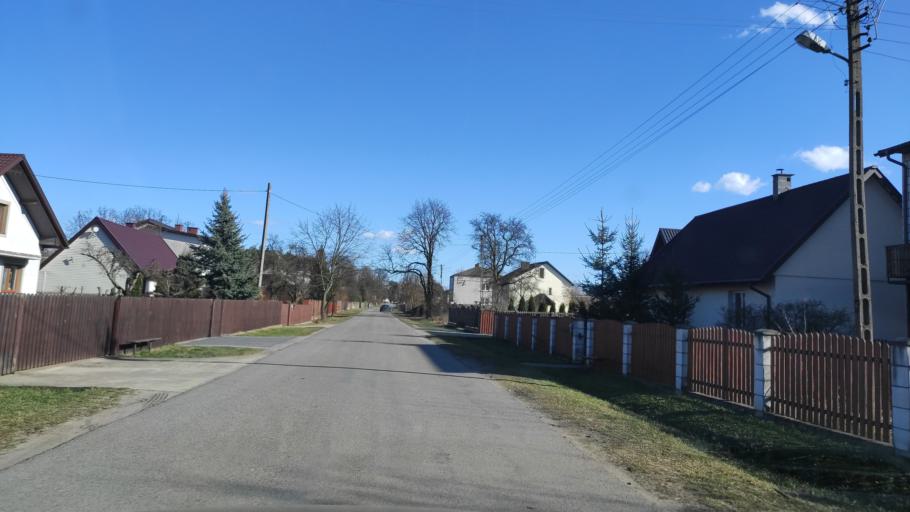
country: PL
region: Masovian Voivodeship
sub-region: Powiat radomski
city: Jastrzebia
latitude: 51.4578
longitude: 21.2649
